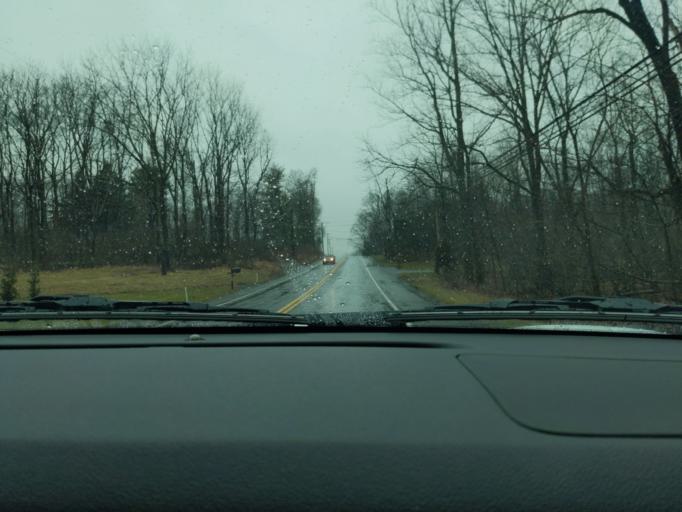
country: US
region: Pennsylvania
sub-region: Bucks County
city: Quakertown
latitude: 40.4335
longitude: -75.3024
